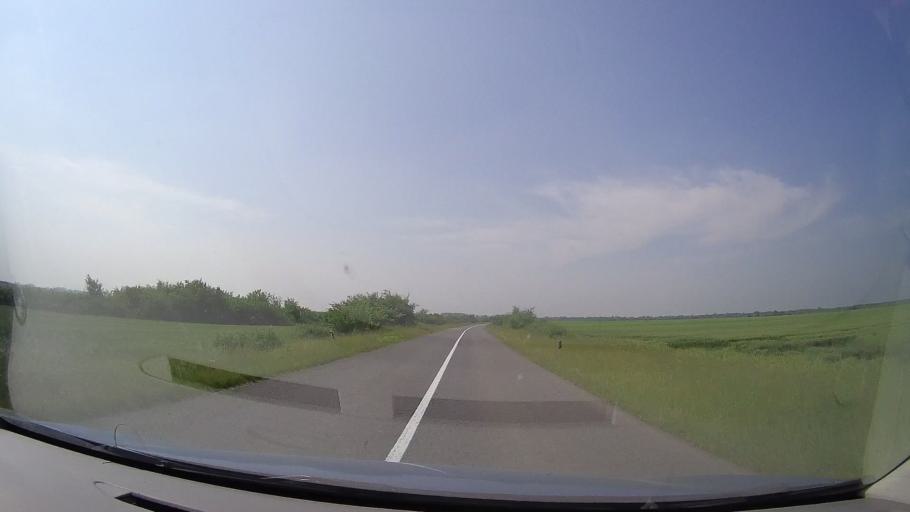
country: RS
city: Jarkovac
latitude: 45.2888
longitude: 20.7644
